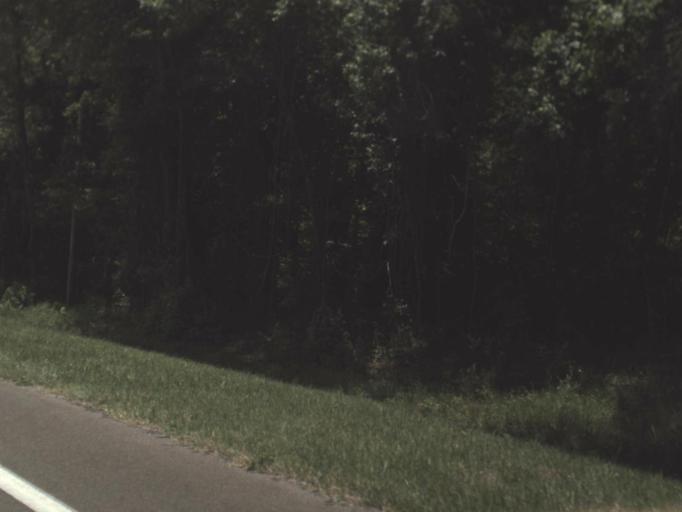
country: US
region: Florida
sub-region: Alachua County
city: Alachua
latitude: 29.8812
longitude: -82.4217
